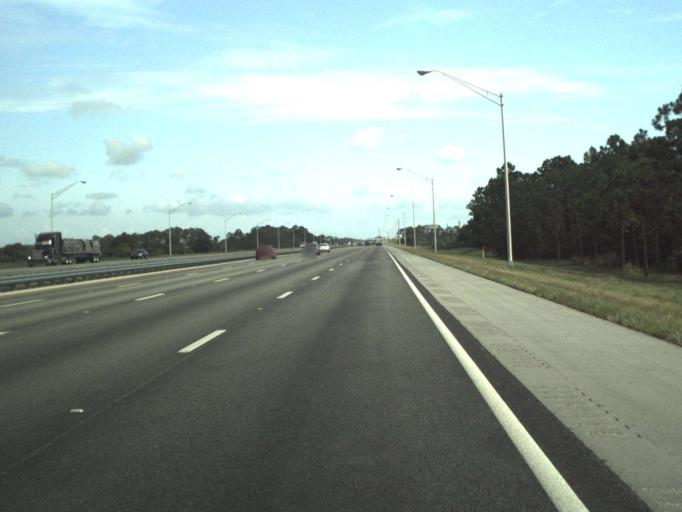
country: US
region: Florida
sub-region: Saint Lucie County
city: Lakewood Park
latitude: 27.4896
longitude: -80.4369
